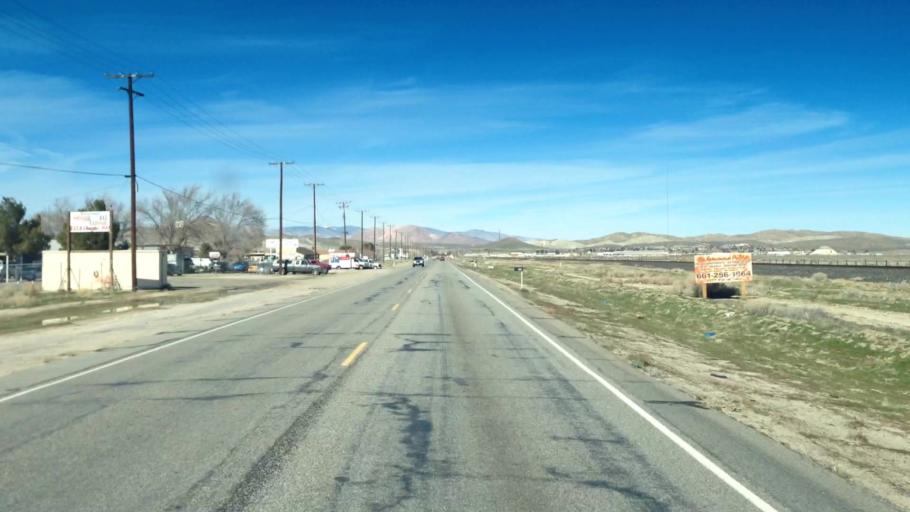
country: US
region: California
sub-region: Kern County
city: Rosamond
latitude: 34.8369
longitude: -118.1586
